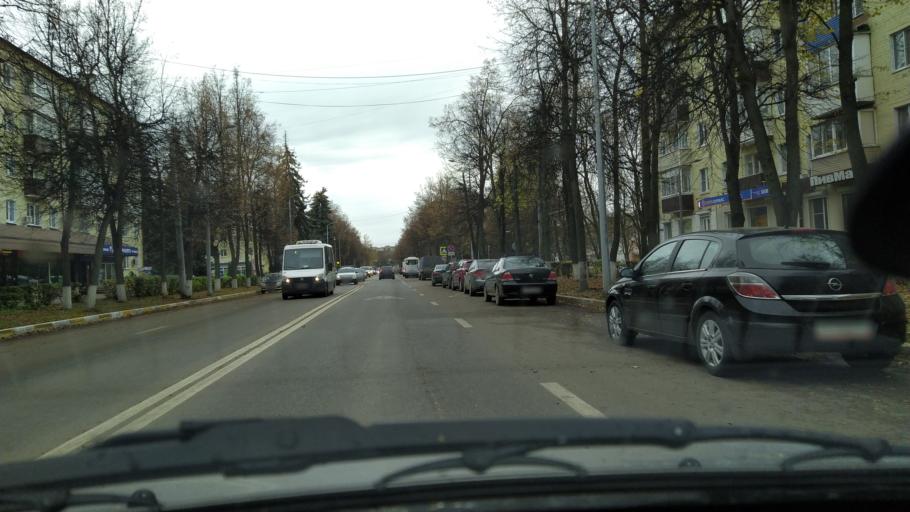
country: RU
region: Moskovskaya
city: Voskresensk
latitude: 55.3244
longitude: 38.6605
